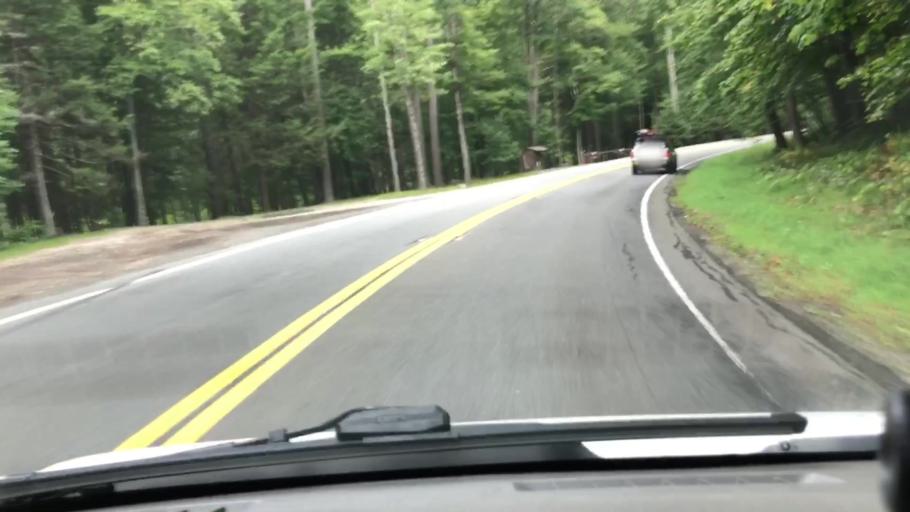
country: US
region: Massachusetts
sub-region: Franklin County
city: Charlemont
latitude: 42.6420
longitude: -72.9496
